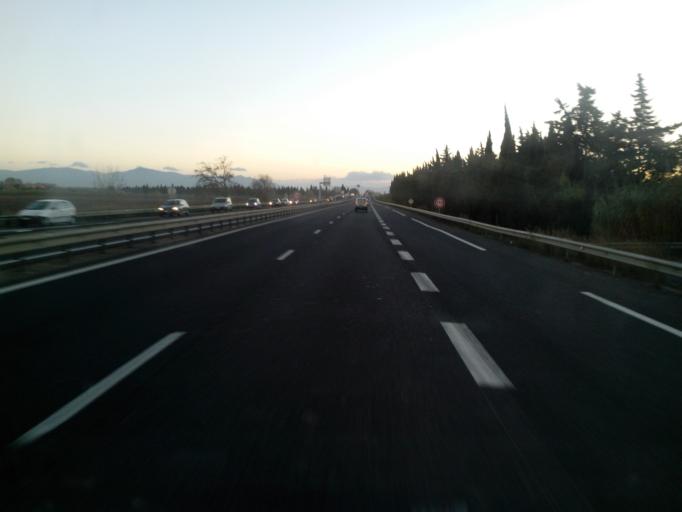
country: FR
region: Languedoc-Roussillon
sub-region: Departement des Pyrenees-Orientales
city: Rivesaltes
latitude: 42.7777
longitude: 2.9027
